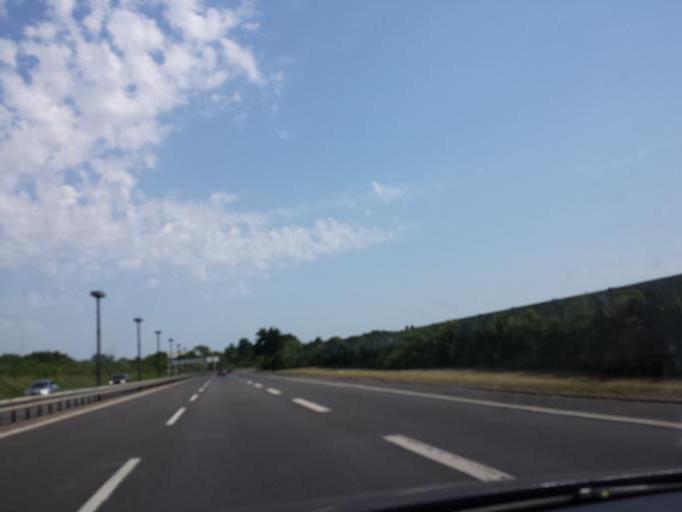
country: DE
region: Berlin
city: Reinickendorf
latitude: 52.5638
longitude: 13.3160
